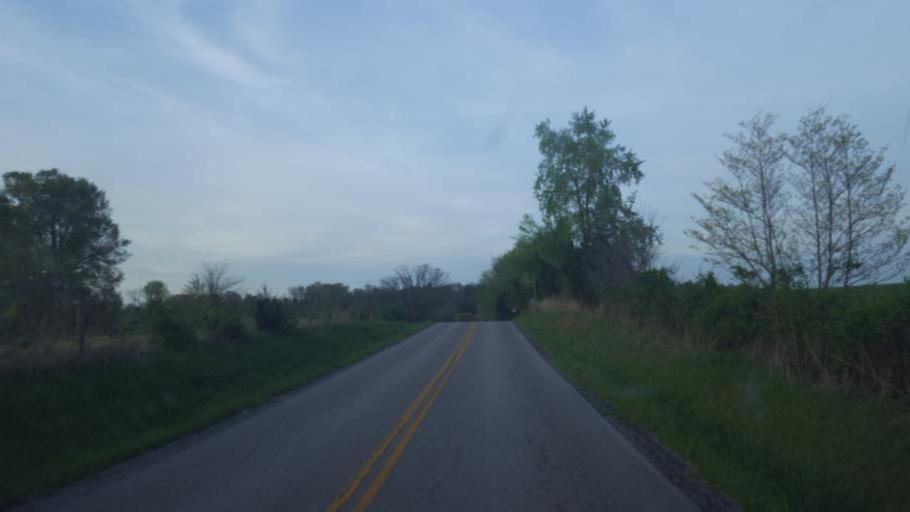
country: US
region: Kentucky
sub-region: Metcalfe County
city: Edmonton
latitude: 37.0847
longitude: -85.6991
